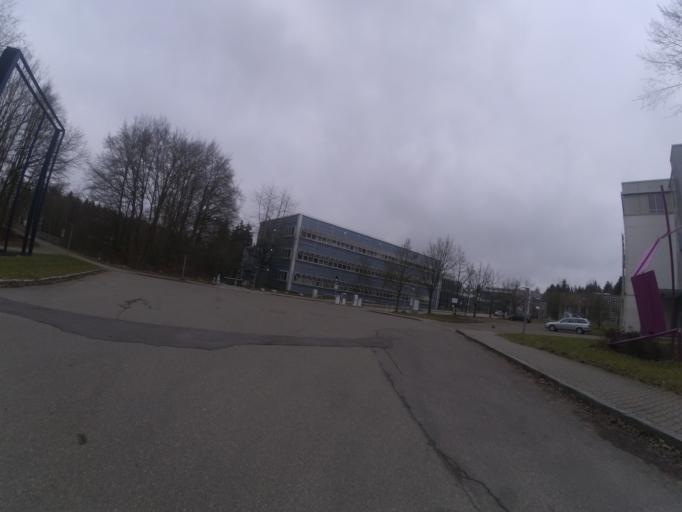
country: DE
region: Baden-Wuerttemberg
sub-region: Tuebingen Region
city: Ulm
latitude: 48.4261
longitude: 9.9619
